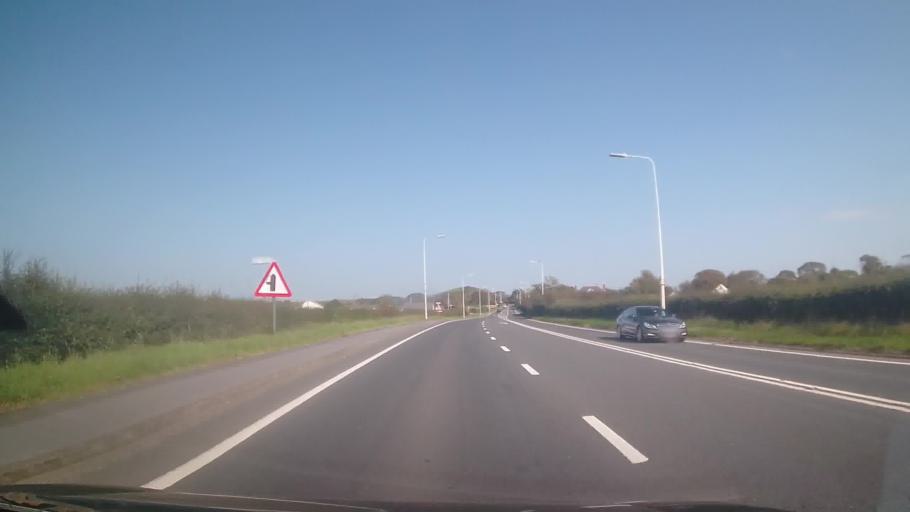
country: GB
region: Wales
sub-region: County of Ceredigion
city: Cardigan
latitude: 52.0924
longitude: -4.6389
